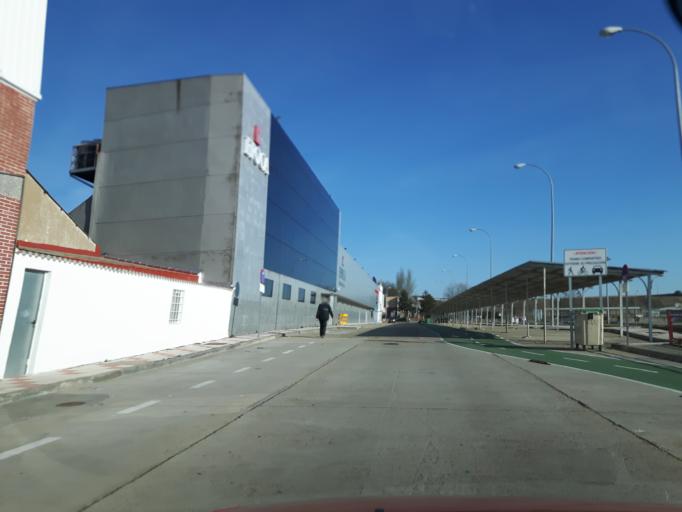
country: ES
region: Castille and Leon
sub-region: Provincia de Salamanca
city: Villares de la Reina
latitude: 40.9893
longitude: -5.6482
